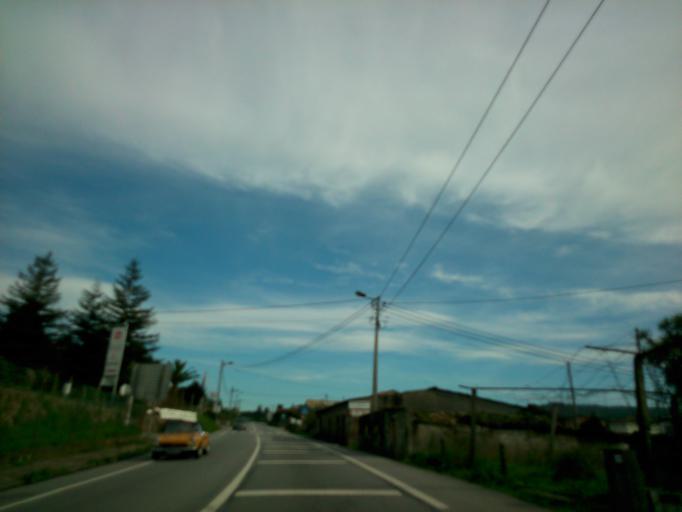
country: PT
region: Braga
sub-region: Barcelos
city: Barcelos
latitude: 41.5197
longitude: -8.5819
